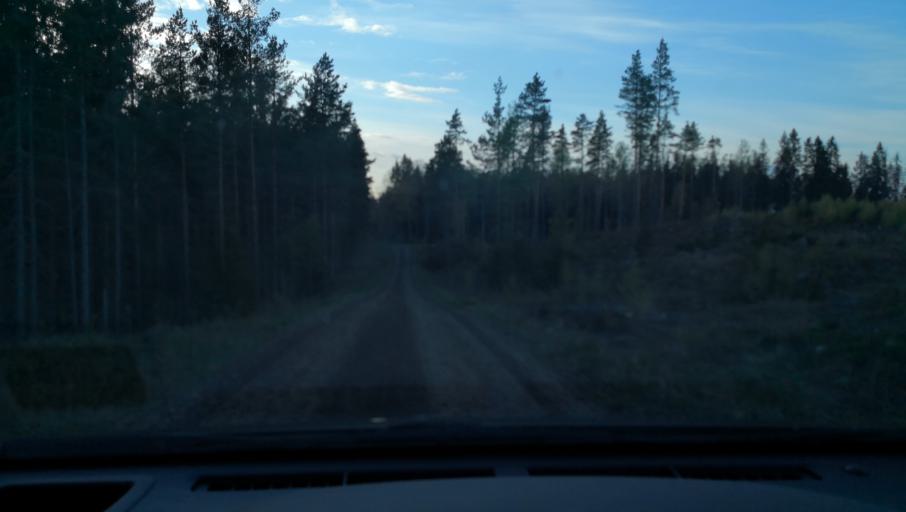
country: SE
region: OErebro
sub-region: Askersunds Kommun
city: Asbro
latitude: 58.8841
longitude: 15.1281
